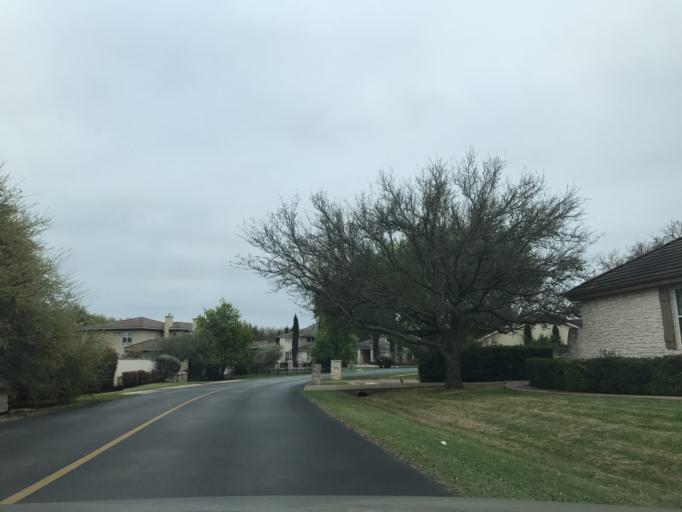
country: US
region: Texas
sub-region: Travis County
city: The Hills
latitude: 30.3466
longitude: -97.9784
